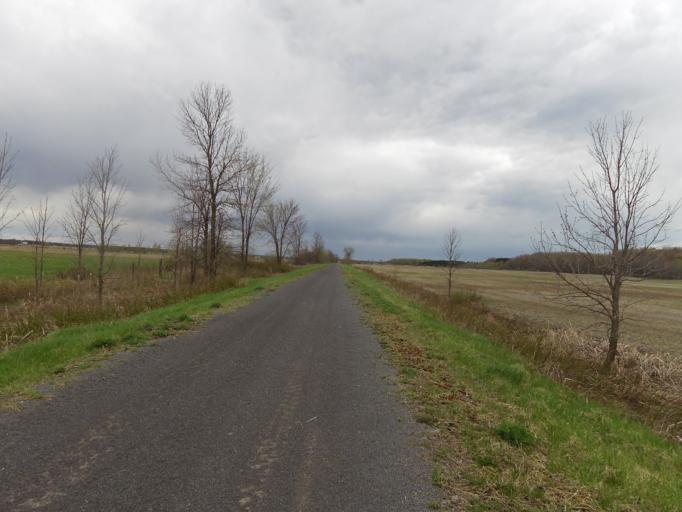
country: CA
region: Quebec
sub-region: Outaouais
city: Papineauville
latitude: 45.5209
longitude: -74.9141
